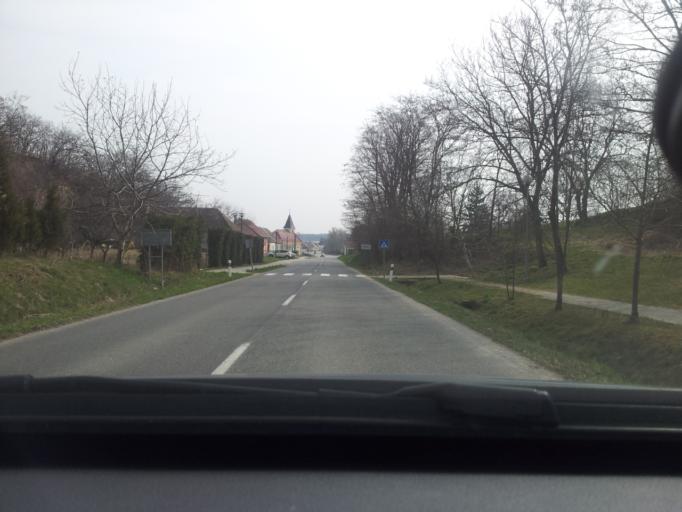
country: SK
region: Trnavsky
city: Leopoldov
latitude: 48.4599
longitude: 17.7123
